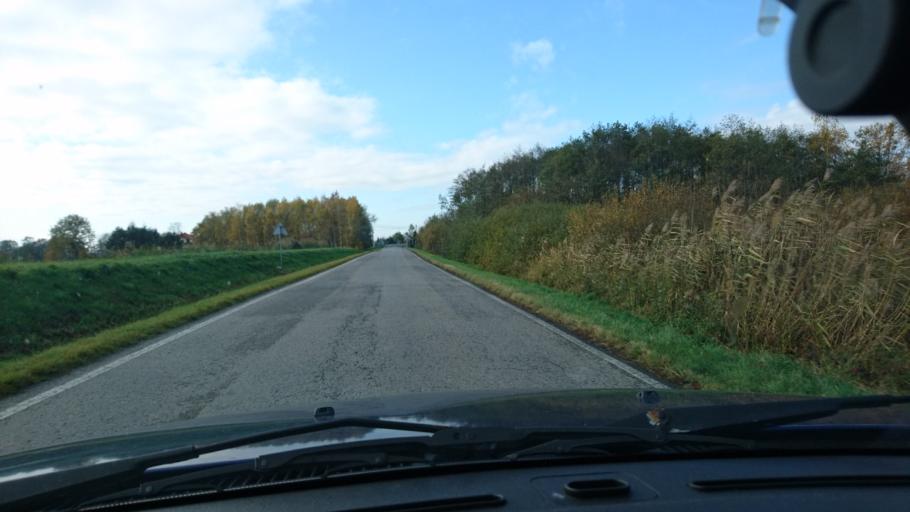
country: PL
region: Lesser Poland Voivodeship
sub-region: Powiat oswiecimski
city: Malec
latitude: 49.9410
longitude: 19.2221
